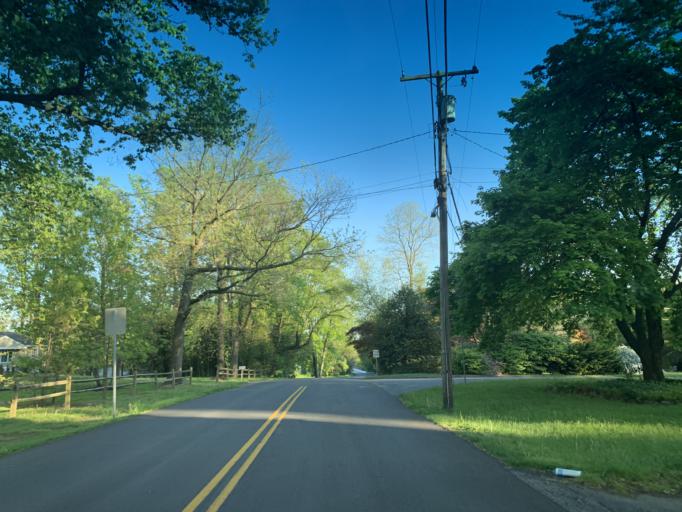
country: US
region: Maryland
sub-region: Harford County
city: Aberdeen
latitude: 39.5372
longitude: -76.1775
